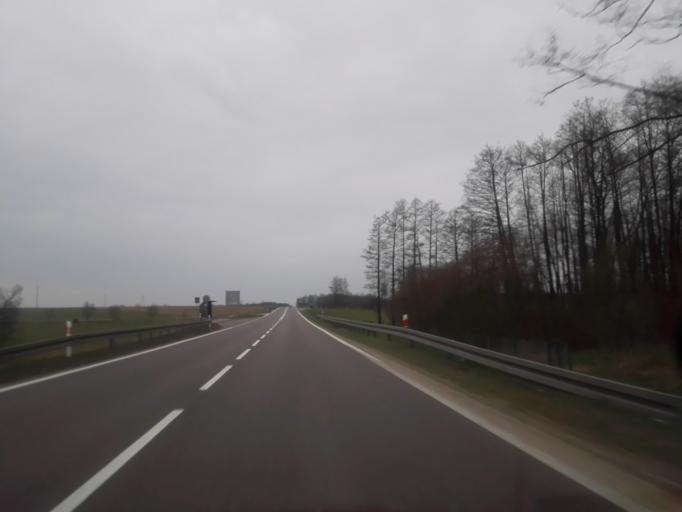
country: PL
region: Podlasie
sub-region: Powiat grajewski
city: Szczuczyn
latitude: 53.5342
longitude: 22.2608
